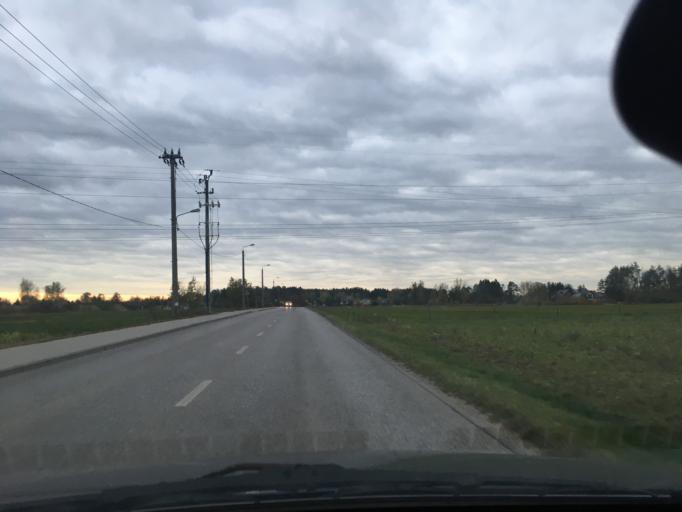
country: PL
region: Masovian Voivodeship
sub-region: Powiat piaseczynski
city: Lesznowola
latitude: 52.0727
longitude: 20.9353
